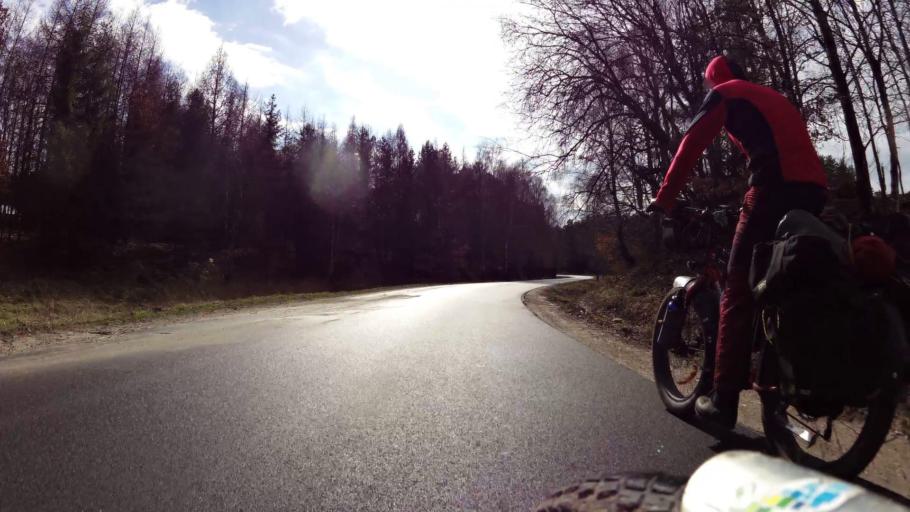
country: PL
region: Pomeranian Voivodeship
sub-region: Powiat bytowski
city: Kolczyglowy
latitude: 54.2075
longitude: 17.2356
